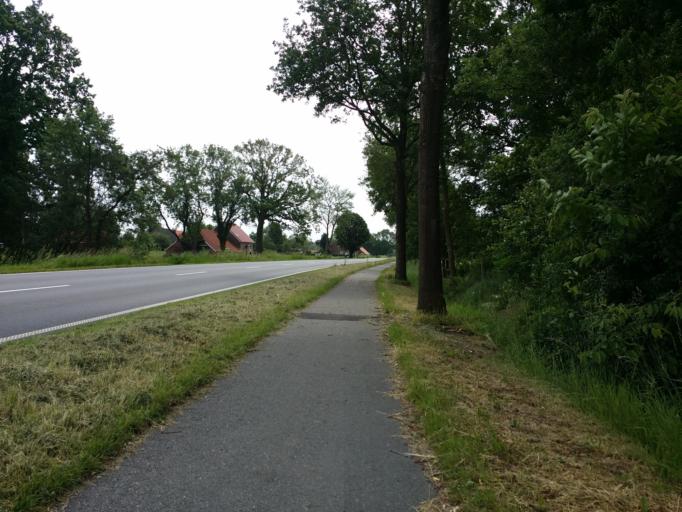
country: DE
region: Lower Saxony
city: Friedeburg
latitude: 53.4302
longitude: 7.8594
